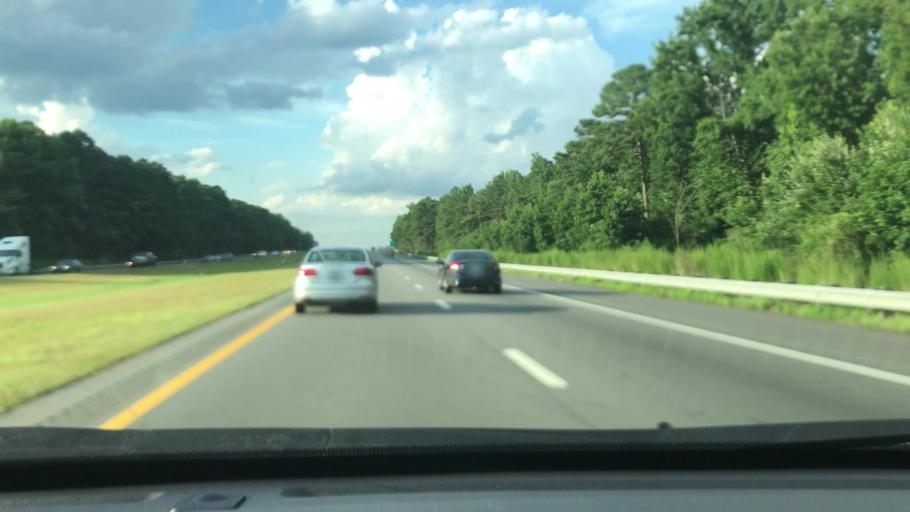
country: US
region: North Carolina
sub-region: Cumberland County
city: Vander
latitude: 35.0277
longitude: -78.8078
